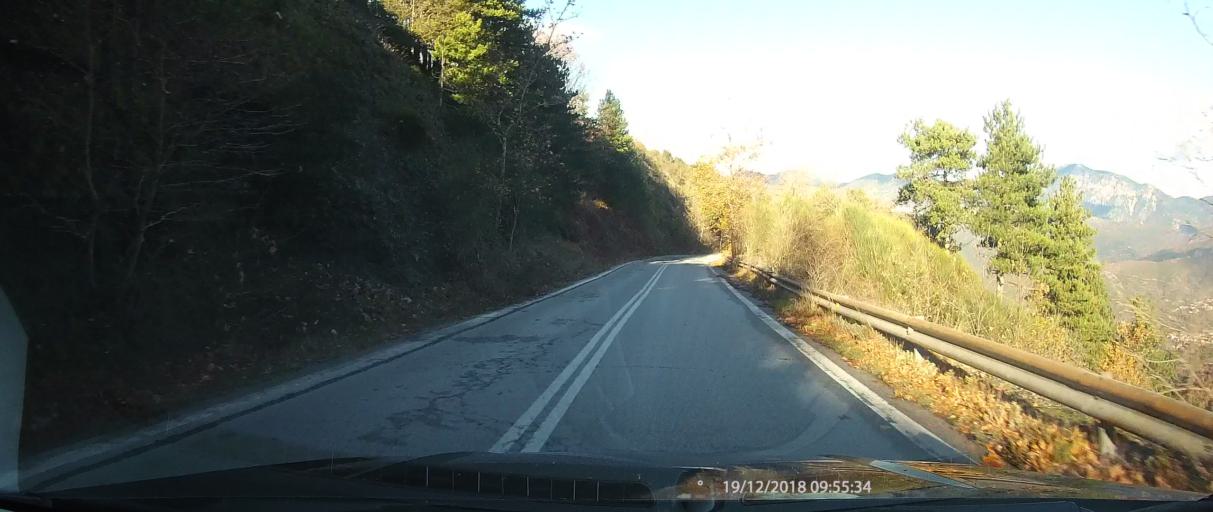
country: GR
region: Peloponnese
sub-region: Nomos Messinias
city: Paralia Vergas
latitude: 37.0821
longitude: 22.2460
